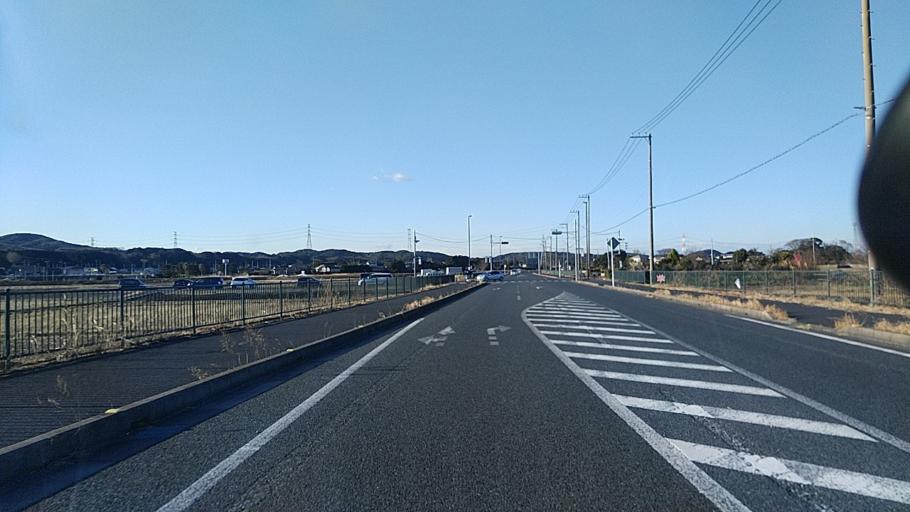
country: JP
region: Chiba
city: Kimitsu
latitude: 35.3253
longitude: 139.8901
